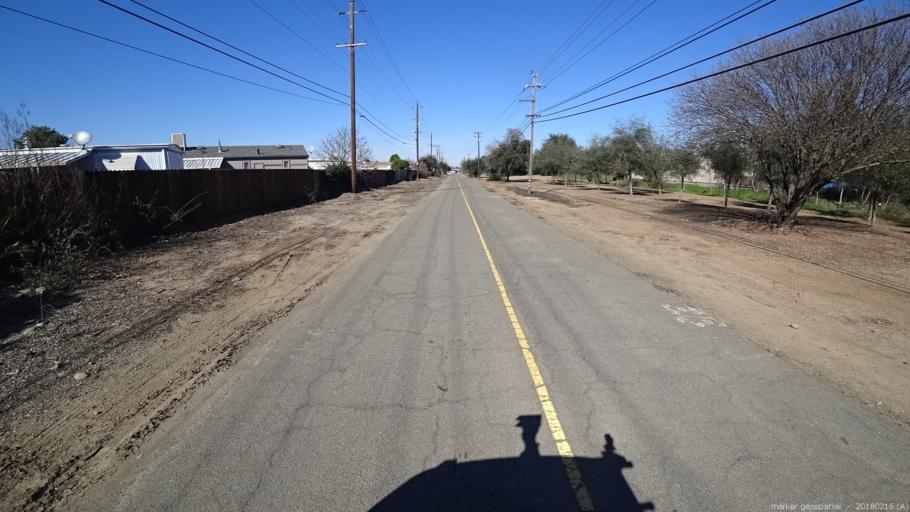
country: US
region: California
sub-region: Sacramento County
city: Gold River
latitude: 38.6152
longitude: -121.2655
